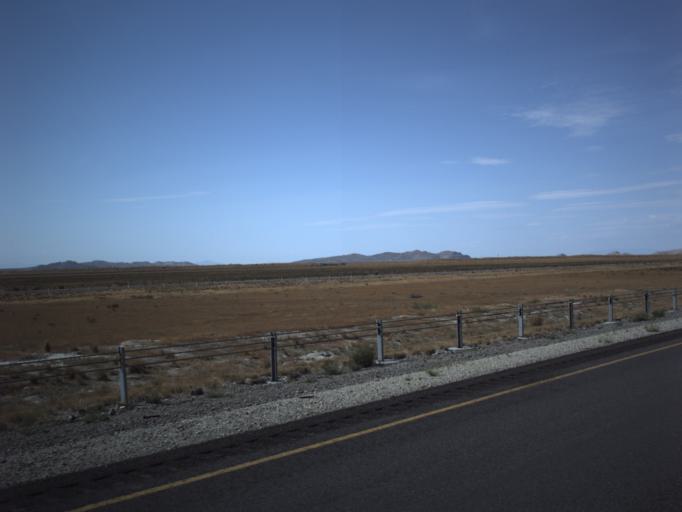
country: US
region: Utah
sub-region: Tooele County
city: Grantsville
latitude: 40.7264
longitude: -113.1816
